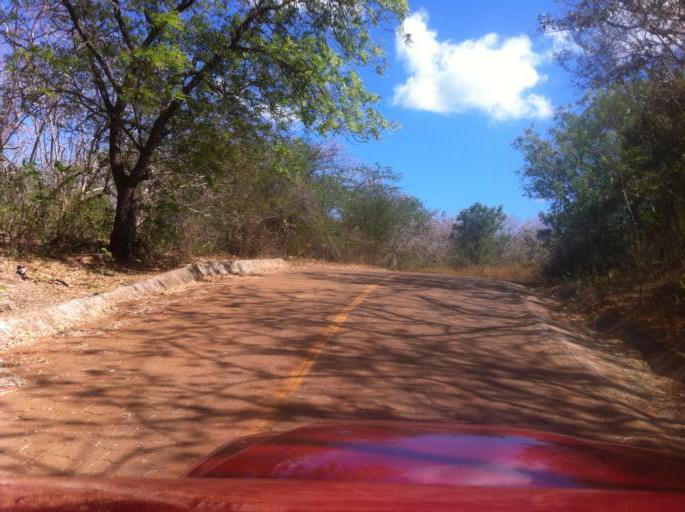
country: NI
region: Carazo
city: Santa Teresa
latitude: 11.6185
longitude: -86.3237
